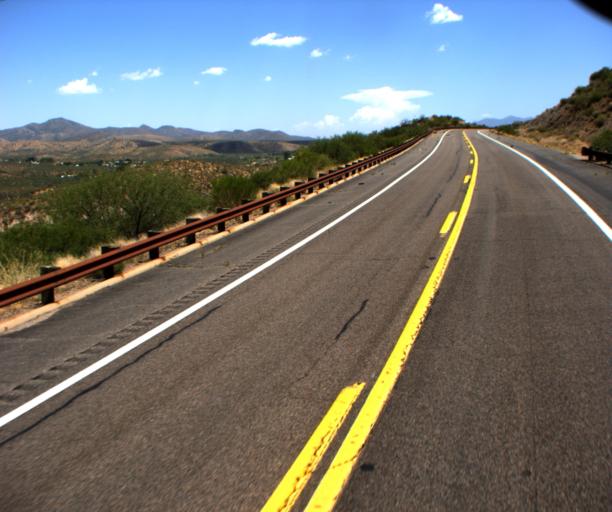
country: US
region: Arizona
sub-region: Gila County
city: Claypool
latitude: 33.5079
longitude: -110.8688
